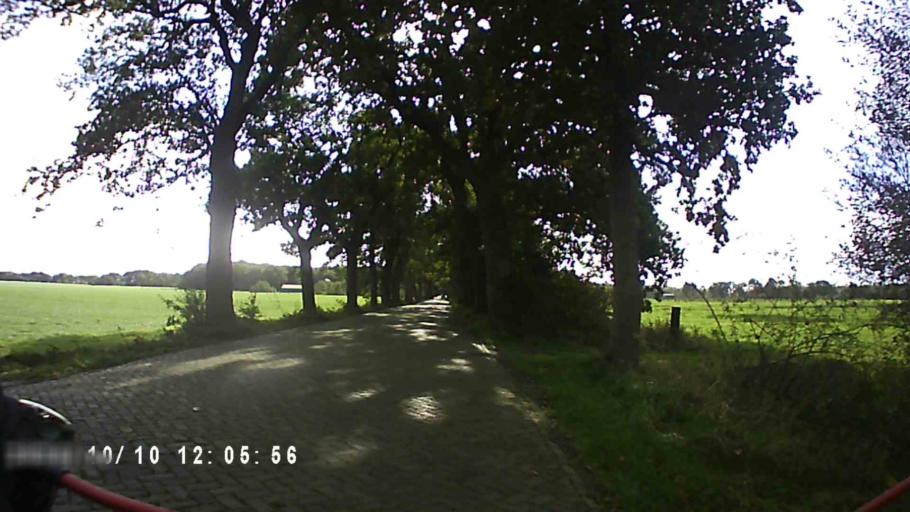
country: NL
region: Friesland
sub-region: Gemeente Heerenveen
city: Jubbega
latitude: 53.0566
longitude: 6.1348
